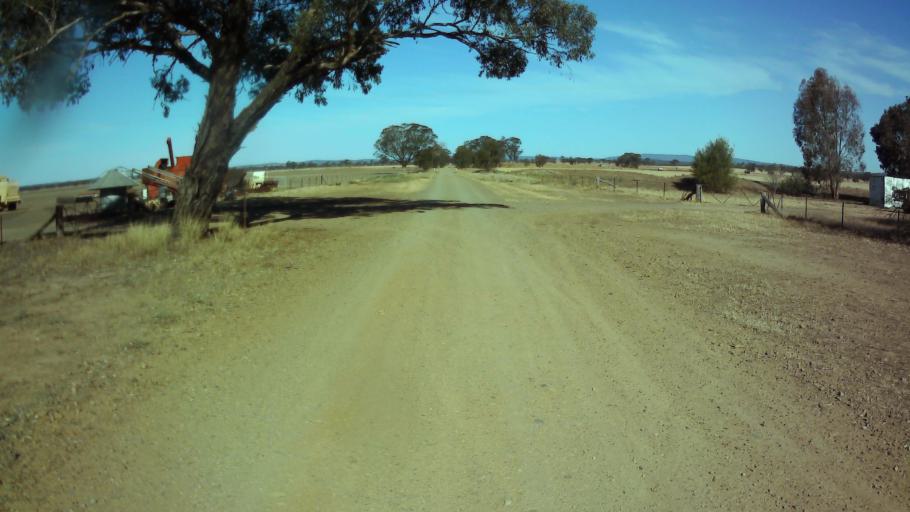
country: AU
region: New South Wales
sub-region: Weddin
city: Grenfell
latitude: -33.6575
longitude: 148.0940
